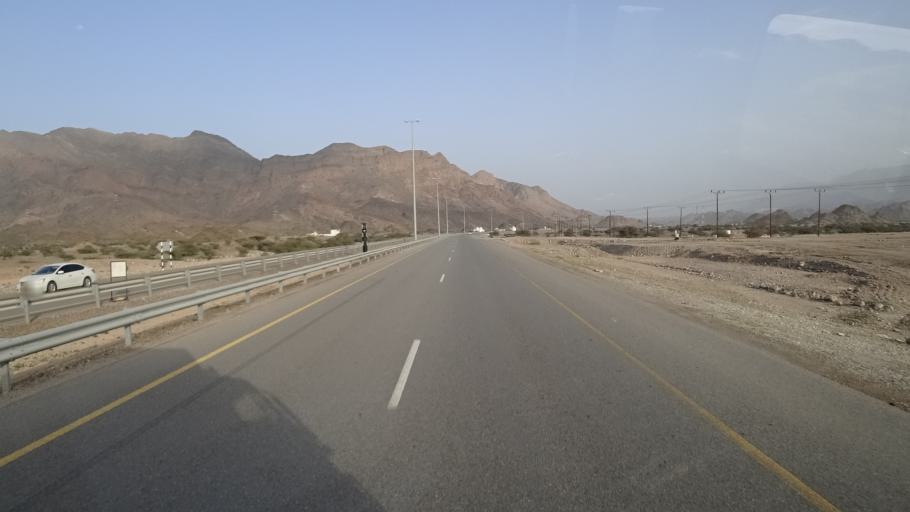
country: OM
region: Muhafazat Masqat
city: Muscat
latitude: 23.3024
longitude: 58.7351
